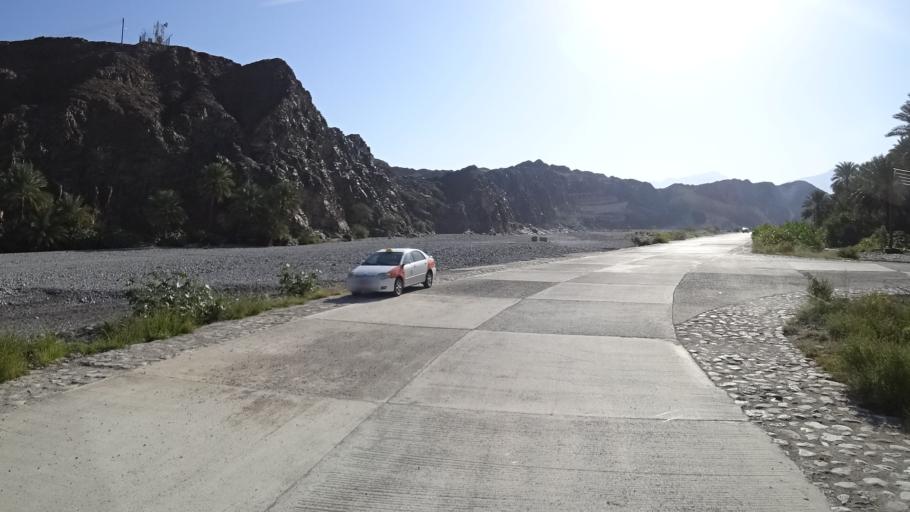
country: OM
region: Al Batinah
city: Bayt al `Awabi
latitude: 23.3851
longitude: 57.6607
